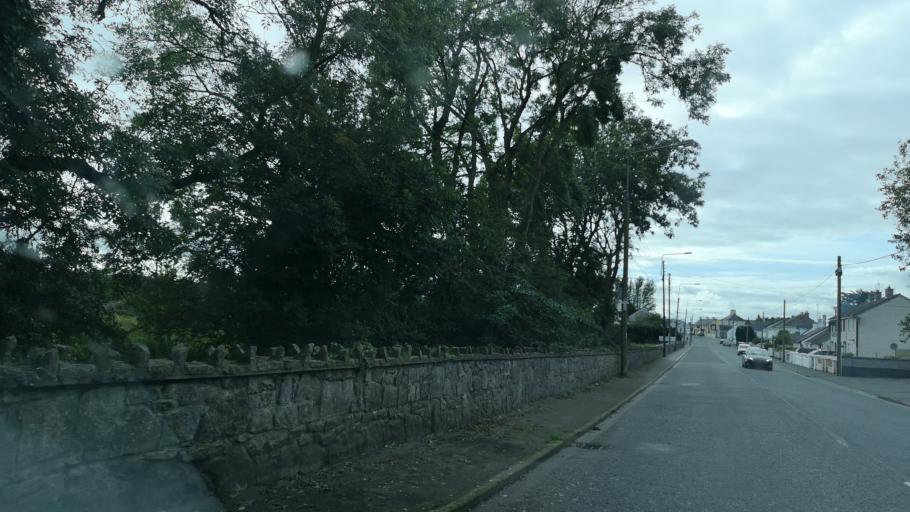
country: IE
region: Leinster
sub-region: Uibh Fhaili
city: Banagher
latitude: 53.2790
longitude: -8.0398
